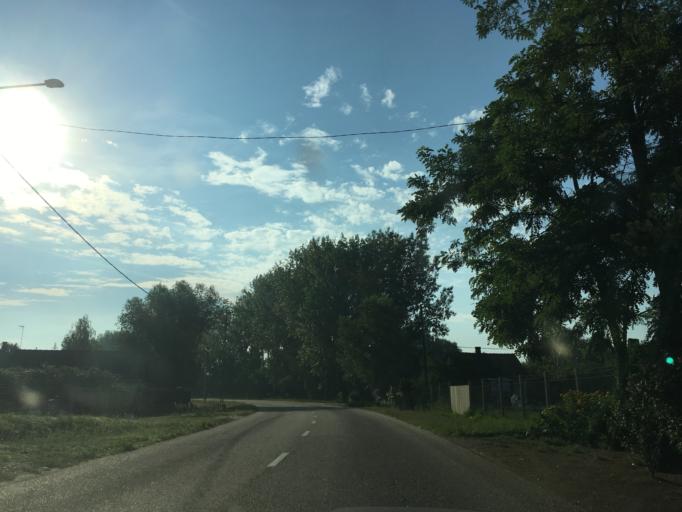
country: HU
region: Hajdu-Bihar
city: Hajdusamson
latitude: 47.5637
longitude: 21.7605
